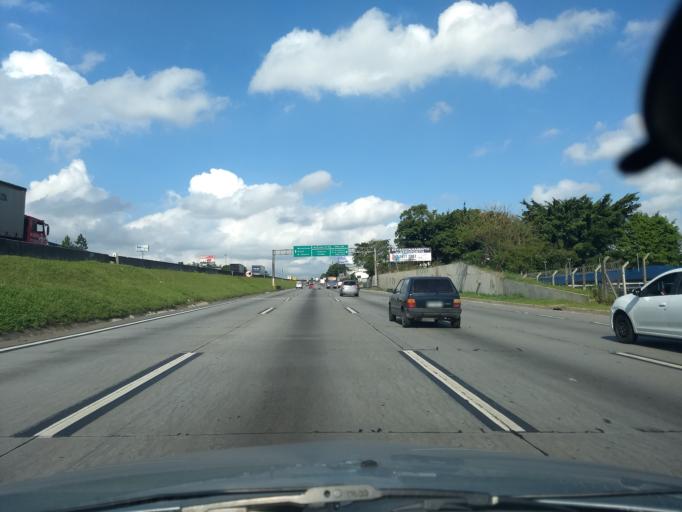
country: BR
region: Sao Paulo
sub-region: Guarulhos
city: Guarulhos
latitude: -23.4585
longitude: -46.4814
